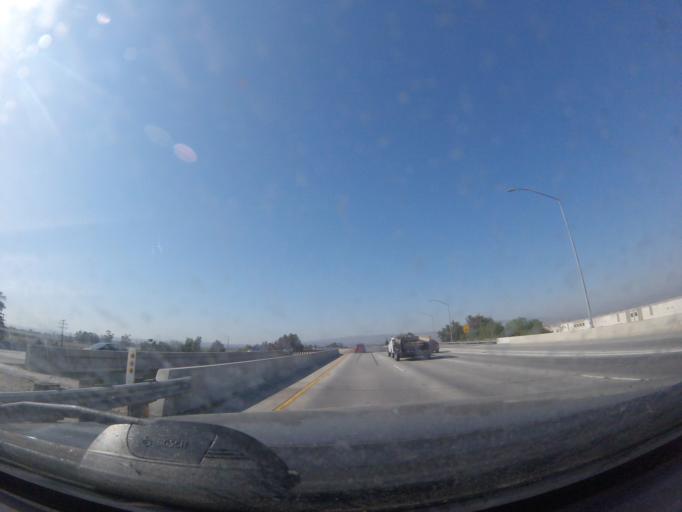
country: US
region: California
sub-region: San Bernardino County
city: Redlands
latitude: 34.0817
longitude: -117.2008
